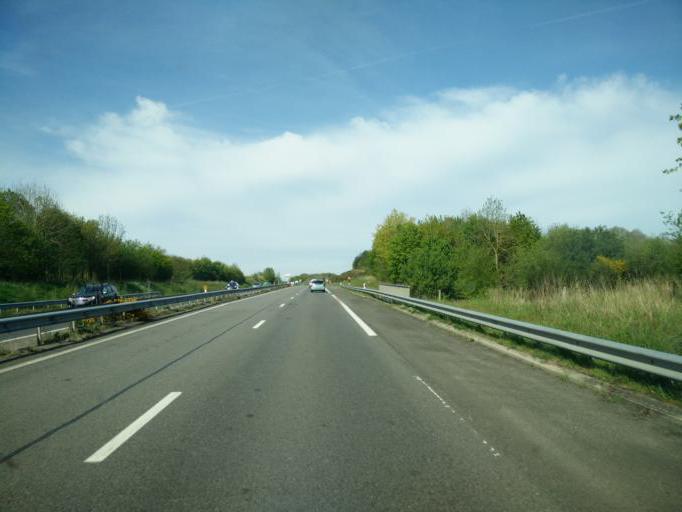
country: FR
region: Brittany
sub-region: Departement d'Ille-et-Vilaine
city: Roz-sur-Couesnon
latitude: 48.5653
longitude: -1.6041
